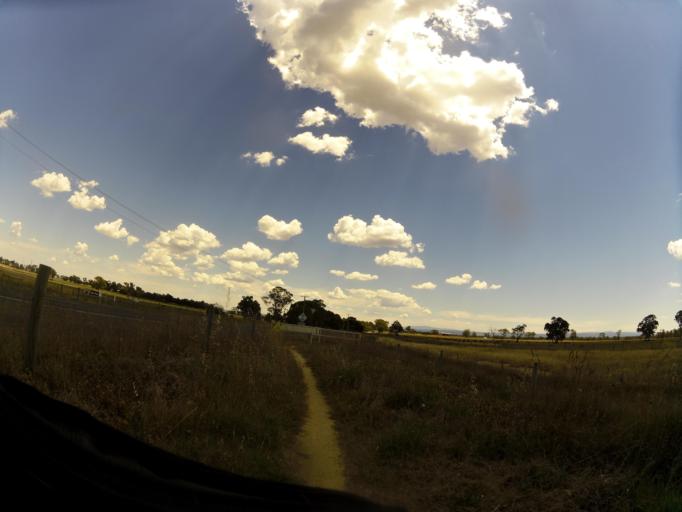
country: AU
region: Victoria
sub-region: Wellington
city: Heyfield
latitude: -37.9835
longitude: 146.8255
